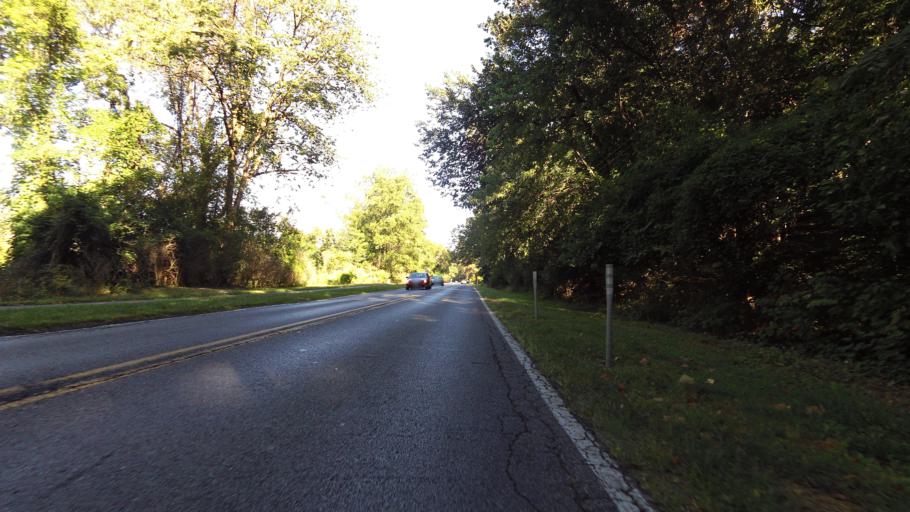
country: US
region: Maryland
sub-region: Montgomery County
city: Brookmont
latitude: 38.9562
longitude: -77.1292
